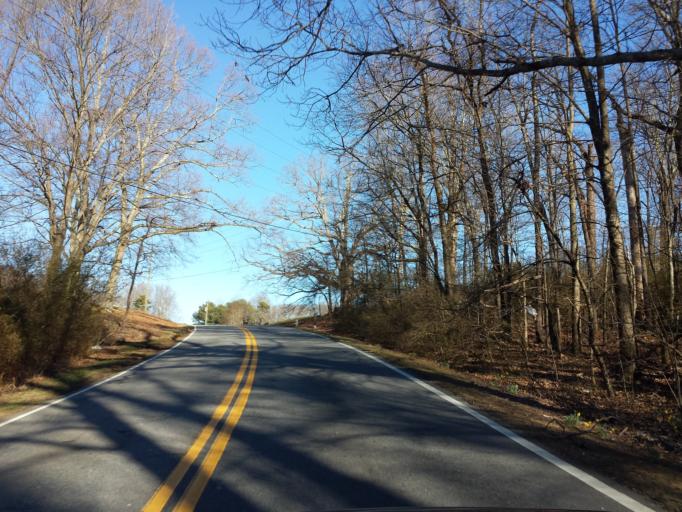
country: US
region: Georgia
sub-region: Cobb County
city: Kennesaw
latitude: 33.9789
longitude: -84.6026
